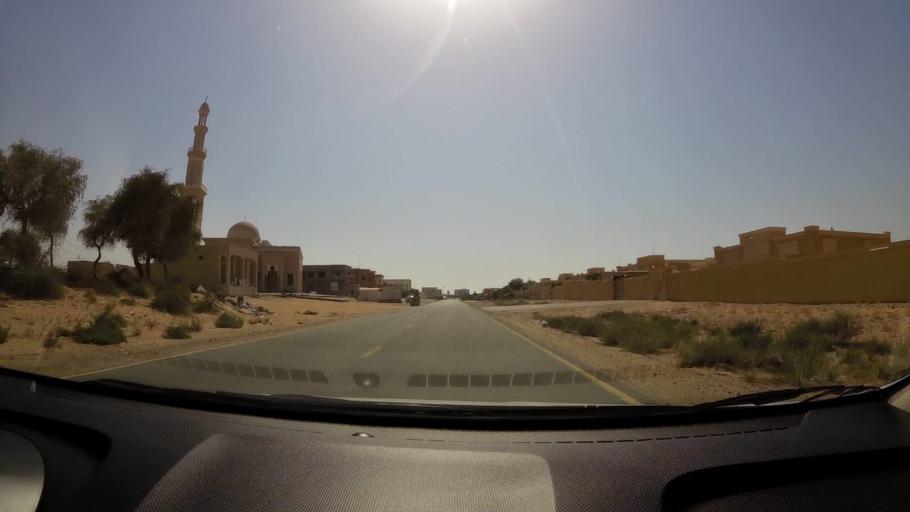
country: AE
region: Umm al Qaywayn
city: Umm al Qaywayn
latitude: 25.4759
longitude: 55.6128
